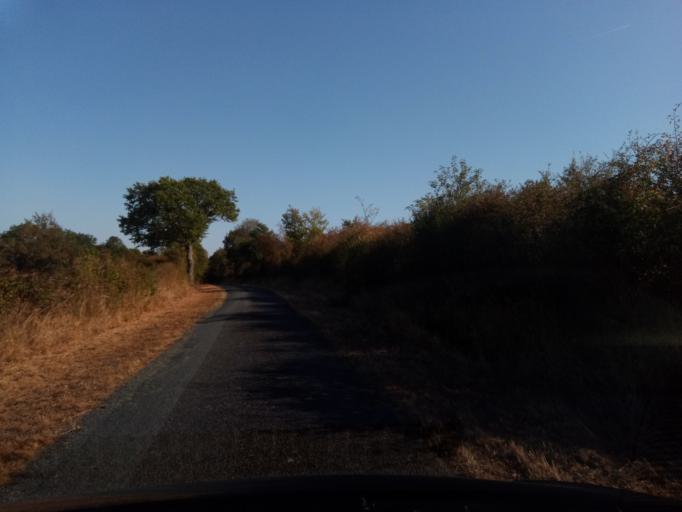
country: FR
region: Poitou-Charentes
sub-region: Departement de la Vienne
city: Saulge
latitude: 46.3711
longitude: 0.8704
